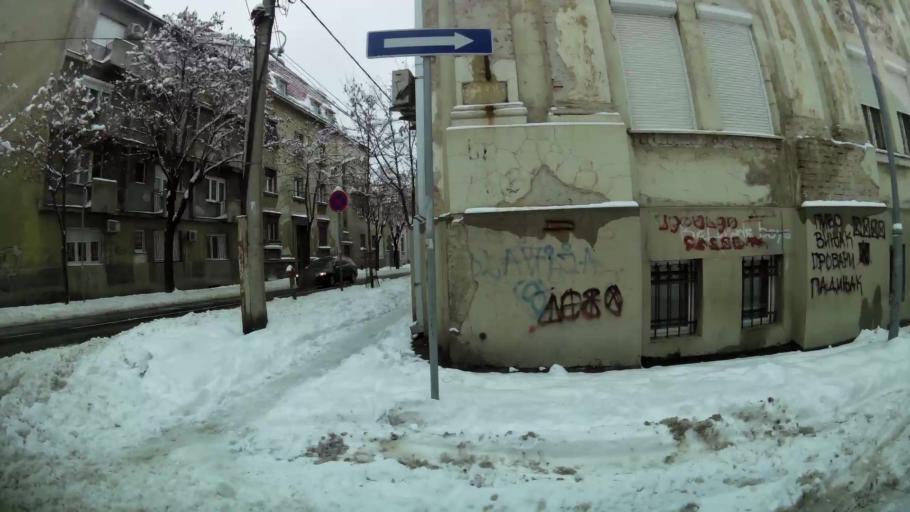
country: RS
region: Central Serbia
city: Belgrade
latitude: 44.8150
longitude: 20.4809
